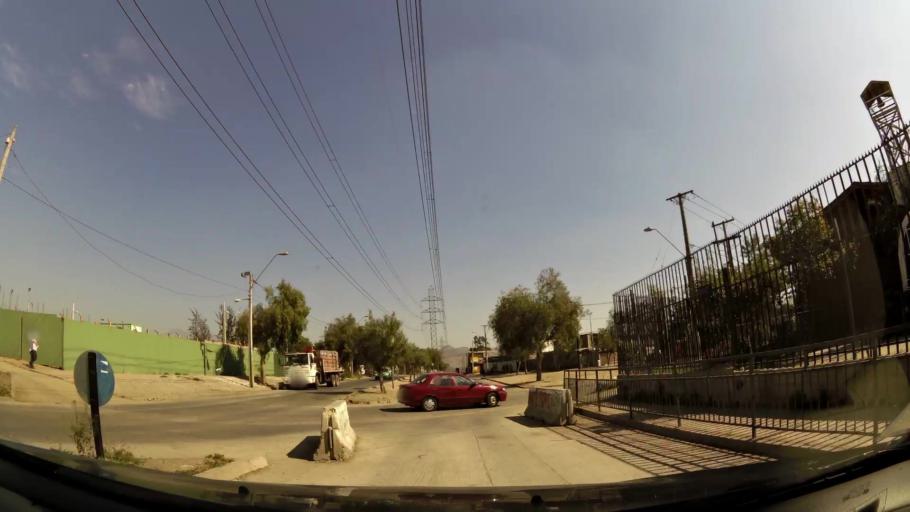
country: CL
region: Santiago Metropolitan
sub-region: Provincia de Santiago
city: La Pintana
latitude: -33.6278
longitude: -70.6242
